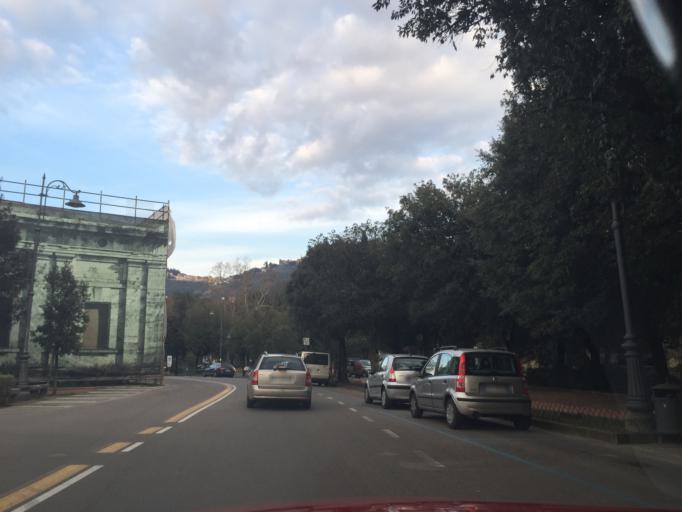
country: IT
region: Tuscany
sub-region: Provincia di Pistoia
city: Montecatini-Terme
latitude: 43.8861
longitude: 10.7753
